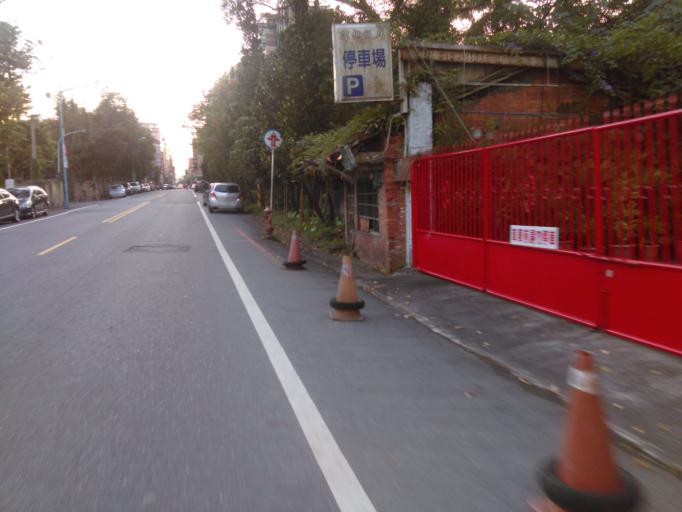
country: TW
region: Taiwan
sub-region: Yilan
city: Yilan
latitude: 24.8283
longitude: 121.7667
